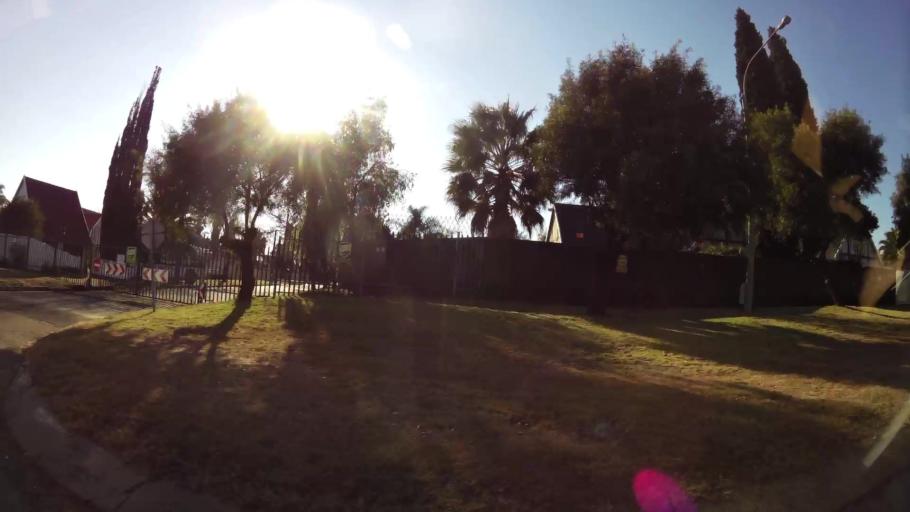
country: ZA
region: Gauteng
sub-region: City of Johannesburg Metropolitan Municipality
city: Modderfontein
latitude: -26.1380
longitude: 28.1679
